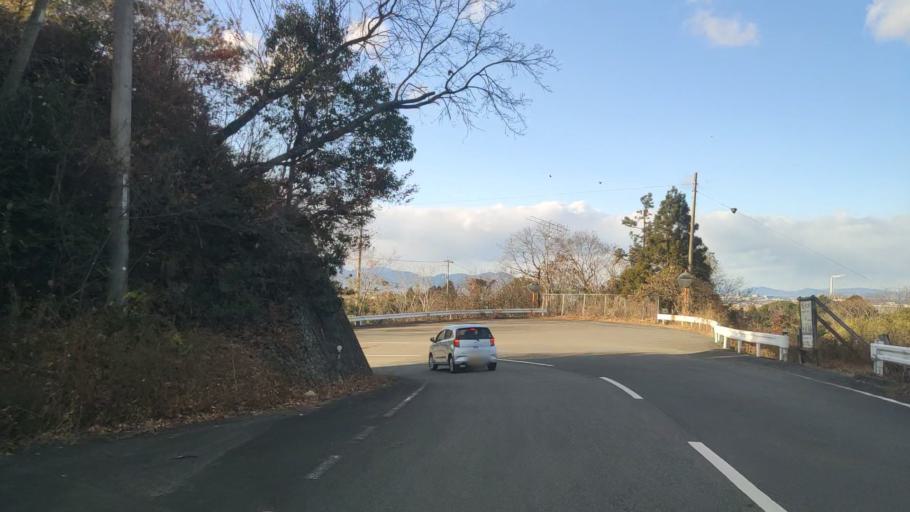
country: JP
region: Ehime
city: Saijo
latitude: 33.8857
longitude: 133.1301
